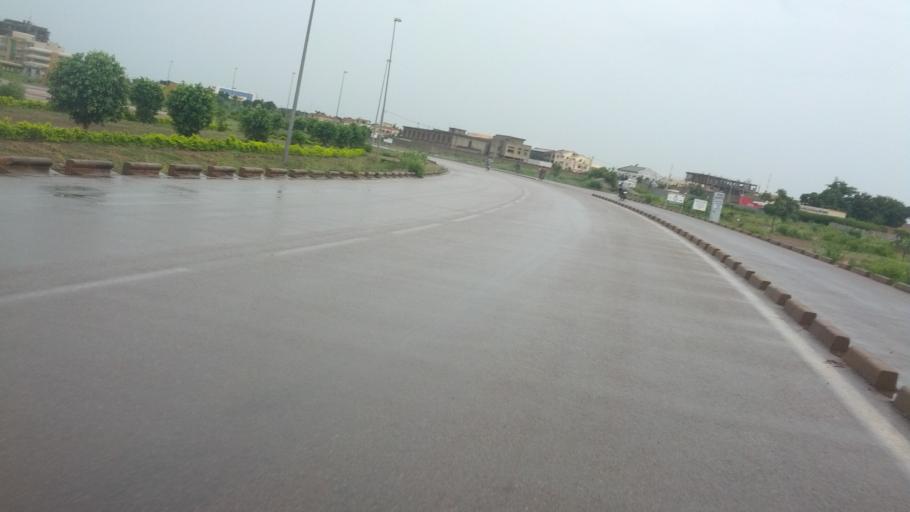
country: BF
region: Centre
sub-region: Kadiogo Province
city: Ouagadougou
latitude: 12.3141
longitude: -1.5043
